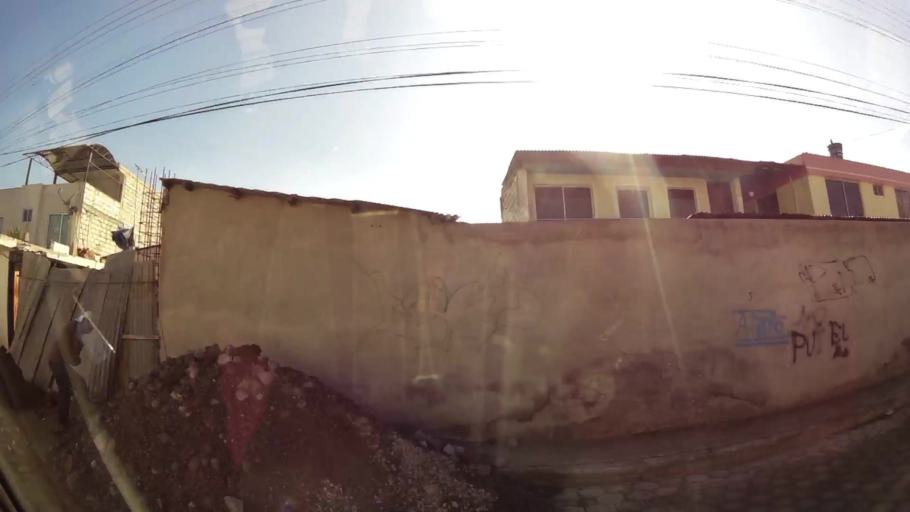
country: EC
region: Chimborazo
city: Riobamba
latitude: -1.6505
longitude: -78.6719
